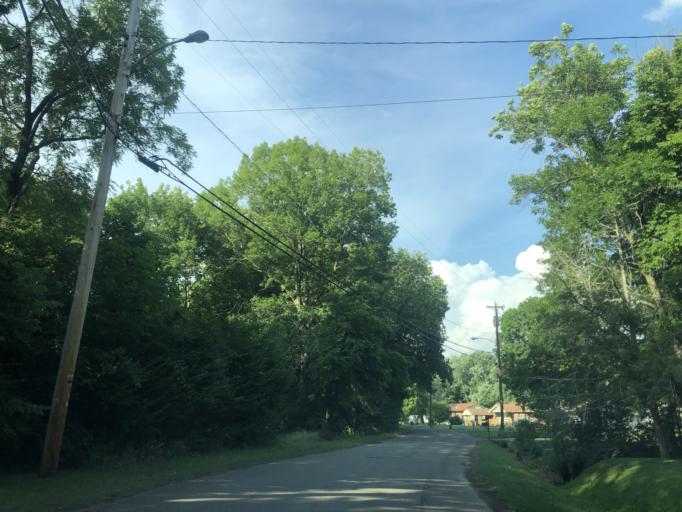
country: US
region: Tennessee
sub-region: Davidson County
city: Nashville
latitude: 36.2331
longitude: -86.7899
